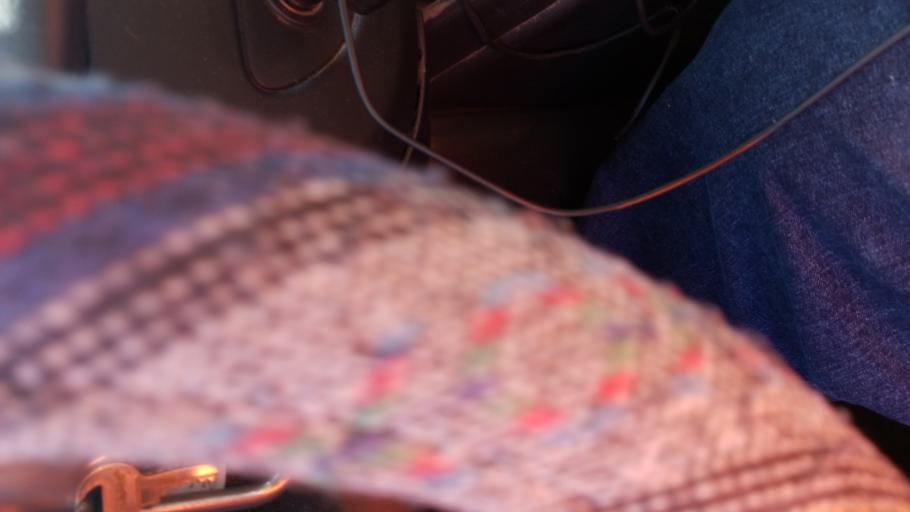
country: US
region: Ohio
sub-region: Hardin County
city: Kenton
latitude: 40.6453
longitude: -83.5941
